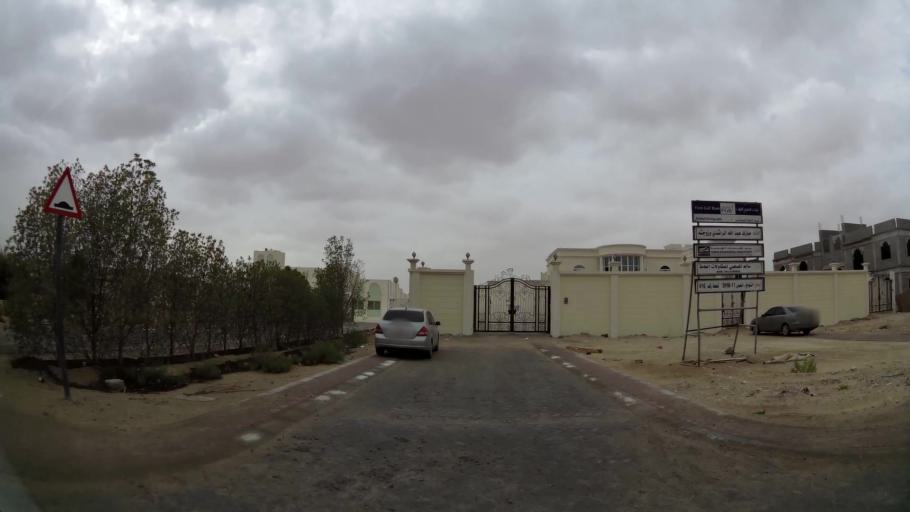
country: AE
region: Abu Dhabi
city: Abu Dhabi
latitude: 24.3299
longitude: 54.6443
